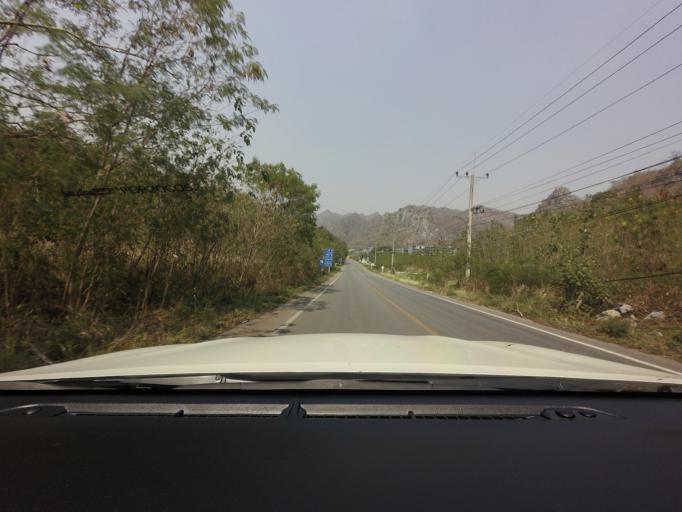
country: TH
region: Sara Buri
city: Muak Lek
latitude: 14.5609
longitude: 101.2983
